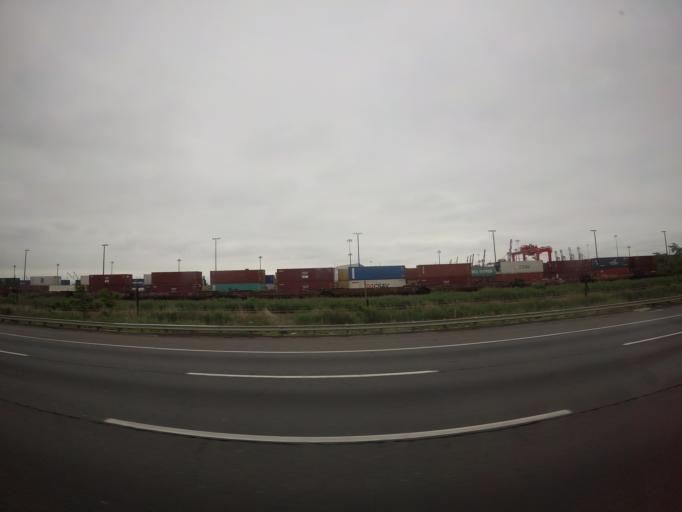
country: US
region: New Jersey
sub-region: Essex County
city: Newark
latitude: 40.6932
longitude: -74.1596
